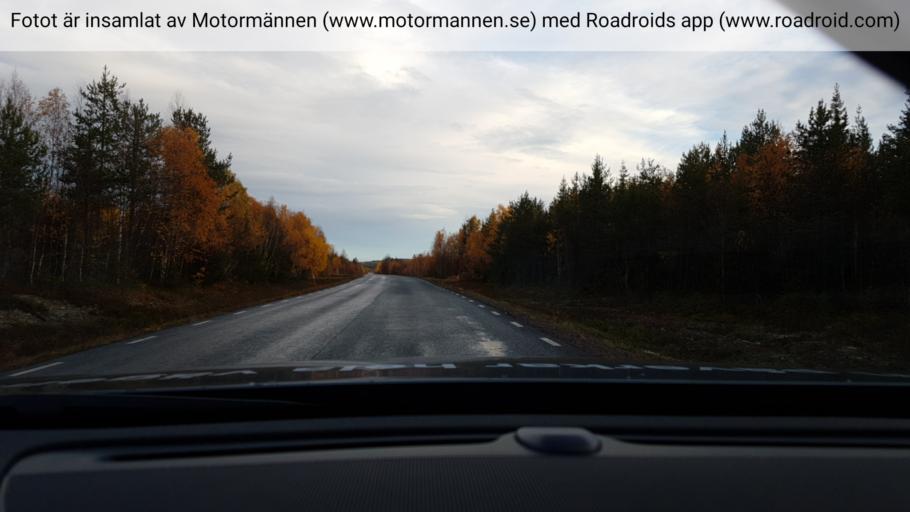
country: SE
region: Norrbotten
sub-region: Overkalix Kommun
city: OEverkalix
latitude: 66.9244
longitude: 22.7430
